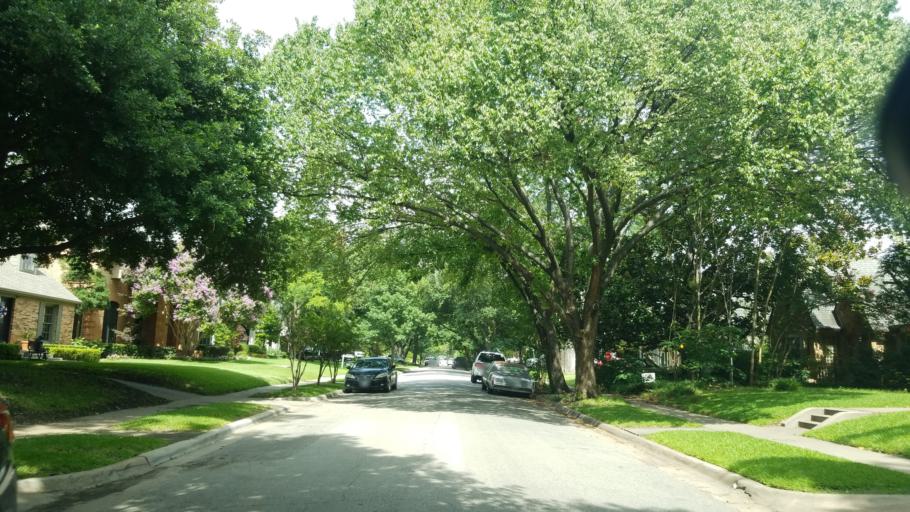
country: US
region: Texas
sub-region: Dallas County
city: University Park
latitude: 32.8539
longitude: -96.7955
